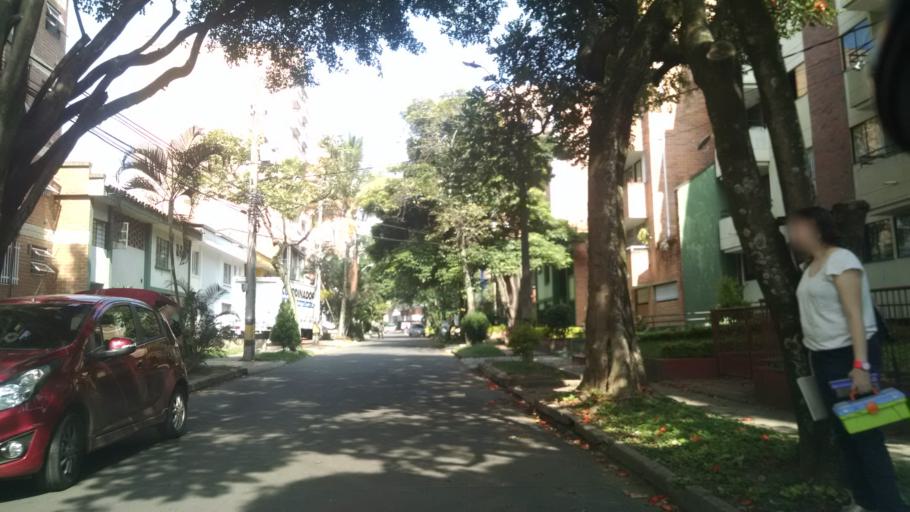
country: CO
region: Antioquia
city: Medellin
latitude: 6.2441
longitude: -75.5861
